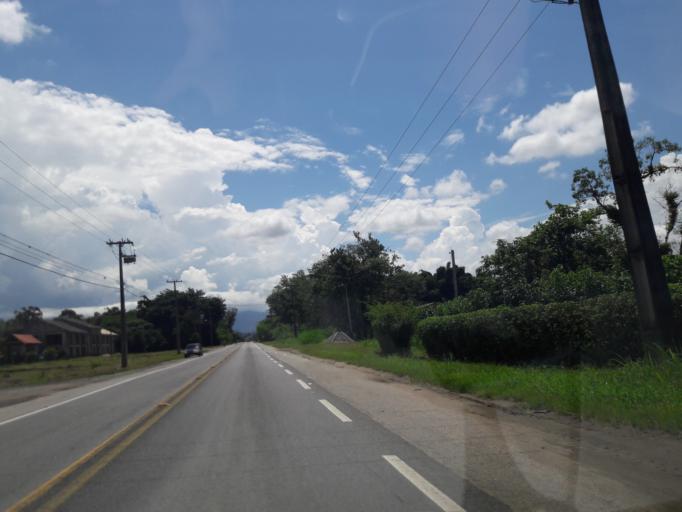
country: BR
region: Parana
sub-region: Antonina
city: Antonina
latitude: -25.5018
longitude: -48.8165
